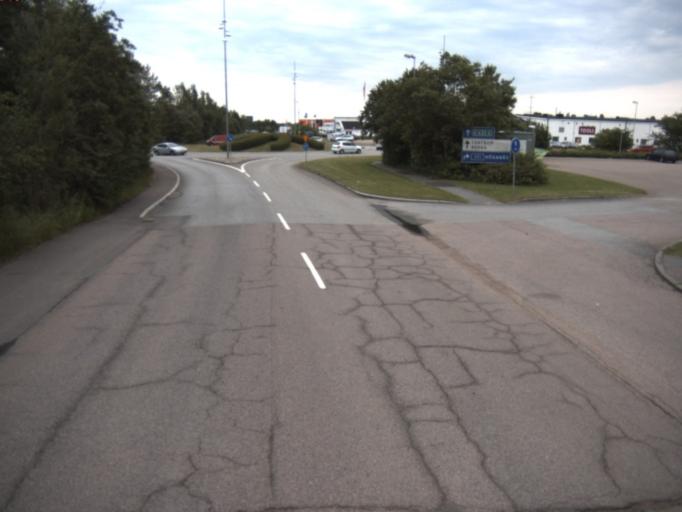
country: SE
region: Skane
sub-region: Helsingborg
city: Odakra
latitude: 56.0814
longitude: 12.7303
